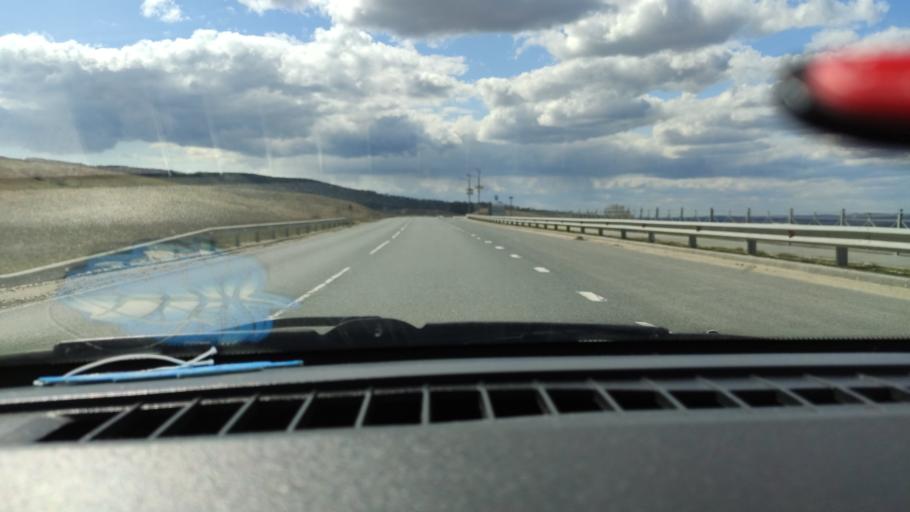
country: RU
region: Saratov
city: Alekseyevka
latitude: 52.3406
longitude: 47.9347
